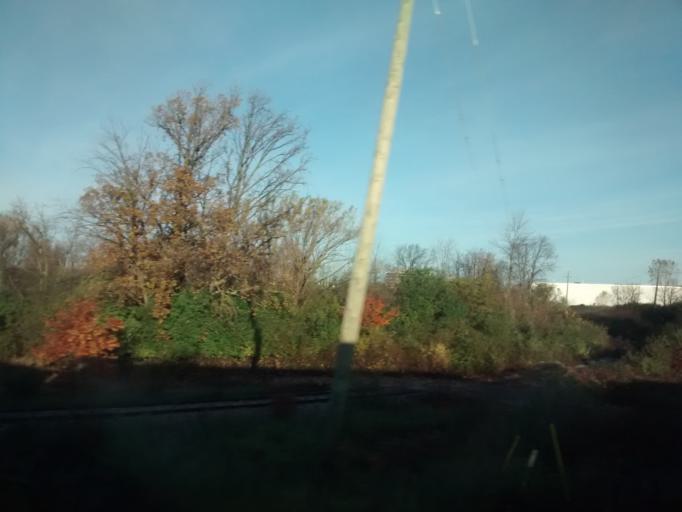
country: CA
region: Ontario
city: Oakville
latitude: 43.4271
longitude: -79.7115
